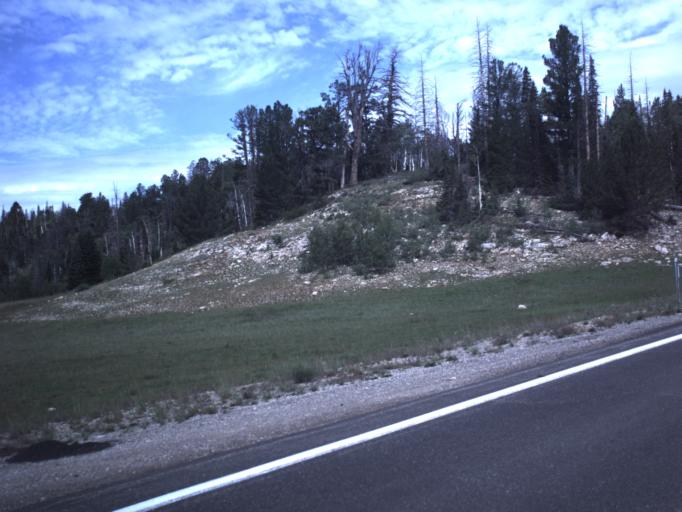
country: US
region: Utah
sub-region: Iron County
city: Parowan
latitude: 37.5429
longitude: -112.7845
